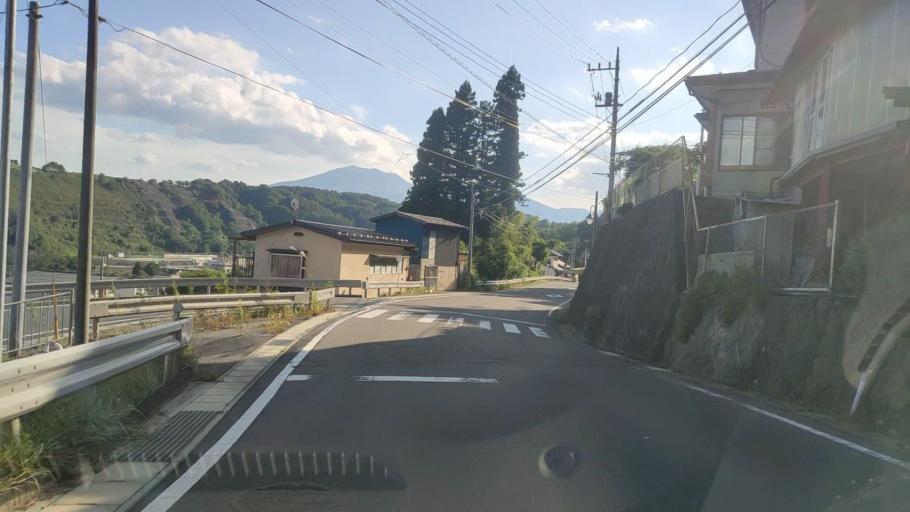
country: JP
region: Nagano
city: Komoro
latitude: 36.5387
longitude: 138.5509
